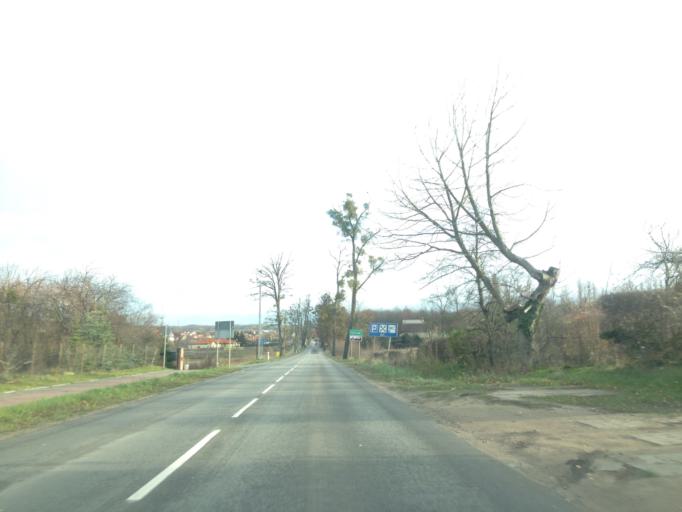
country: PL
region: Pomeranian Voivodeship
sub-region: Powiat gdanski
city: Kolbudy
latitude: 54.2772
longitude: 18.4791
